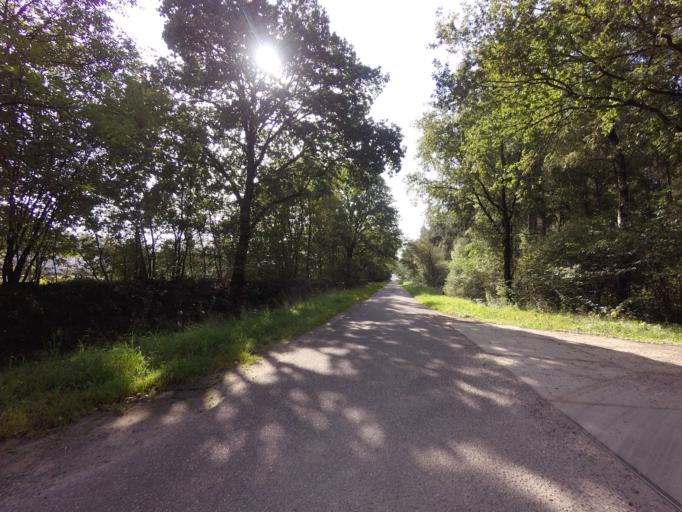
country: NL
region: Drenthe
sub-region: Gemeente Borger-Odoorn
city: Borger
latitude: 52.9384
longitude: 6.6970
